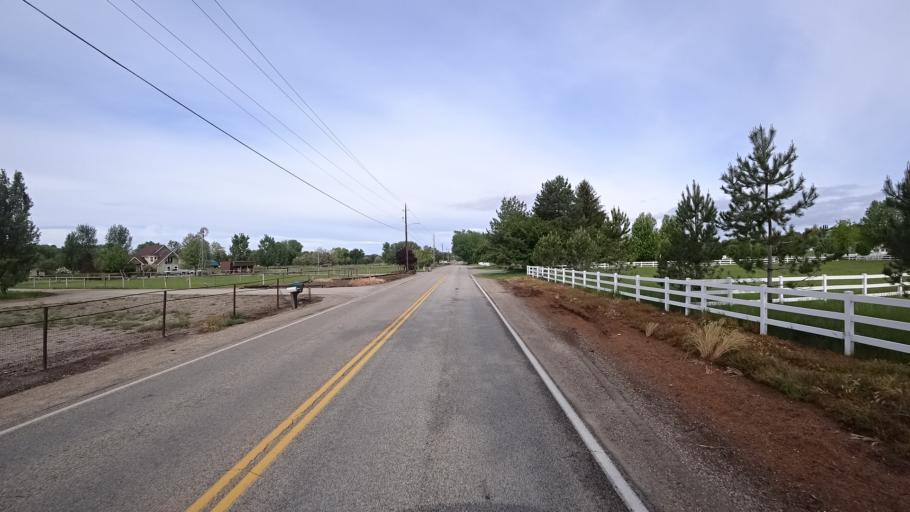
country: US
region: Idaho
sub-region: Ada County
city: Eagle
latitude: 43.7208
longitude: -116.3262
